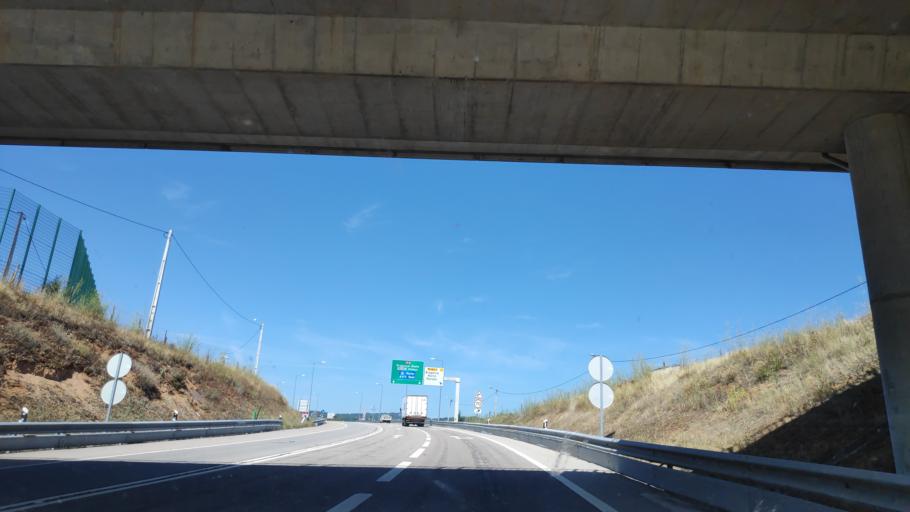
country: PT
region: Braganca
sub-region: Braganca Municipality
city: Braganca
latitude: 41.8210
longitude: -6.7497
